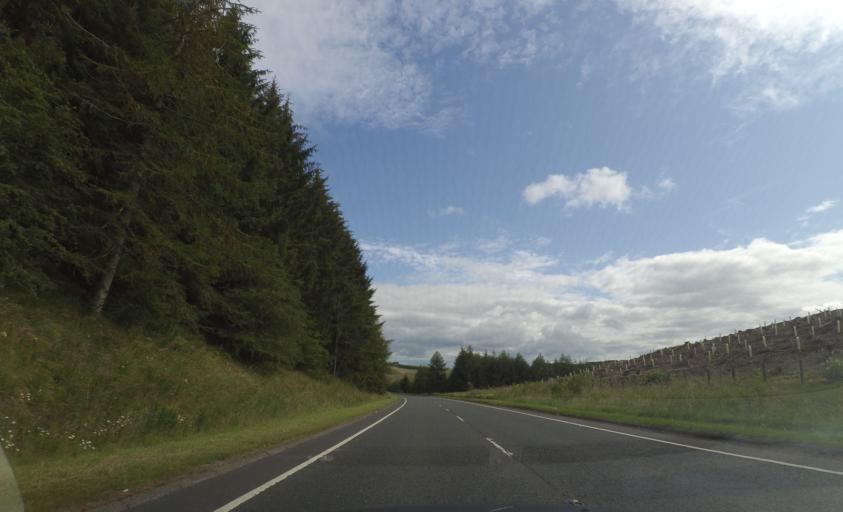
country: GB
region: Scotland
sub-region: The Scottish Borders
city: Selkirk
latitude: 55.5213
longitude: -2.8299
